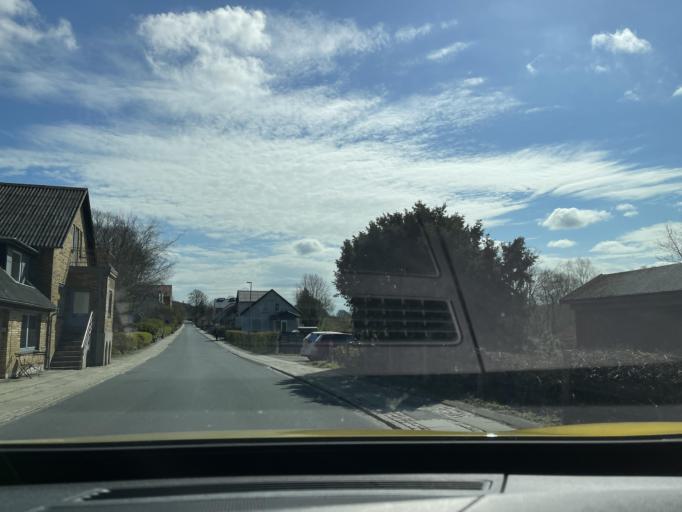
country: DK
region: Central Jutland
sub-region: Favrskov Kommune
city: Hadsten
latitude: 56.3262
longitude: 10.0508
